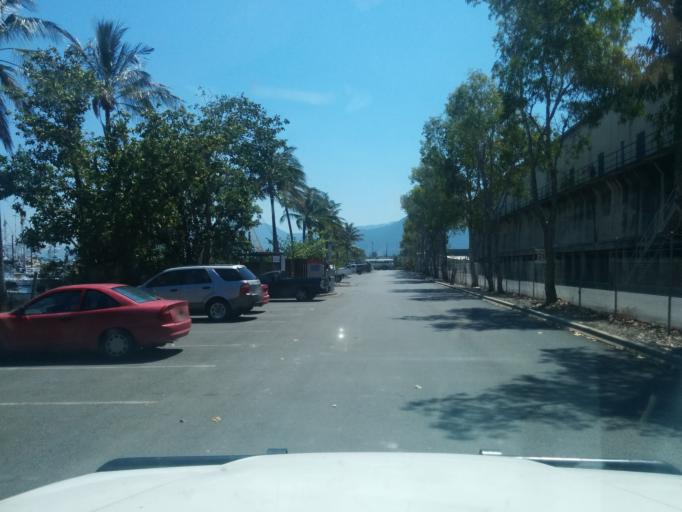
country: AU
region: Queensland
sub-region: Cairns
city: Cairns
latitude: -16.9402
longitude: 145.7768
